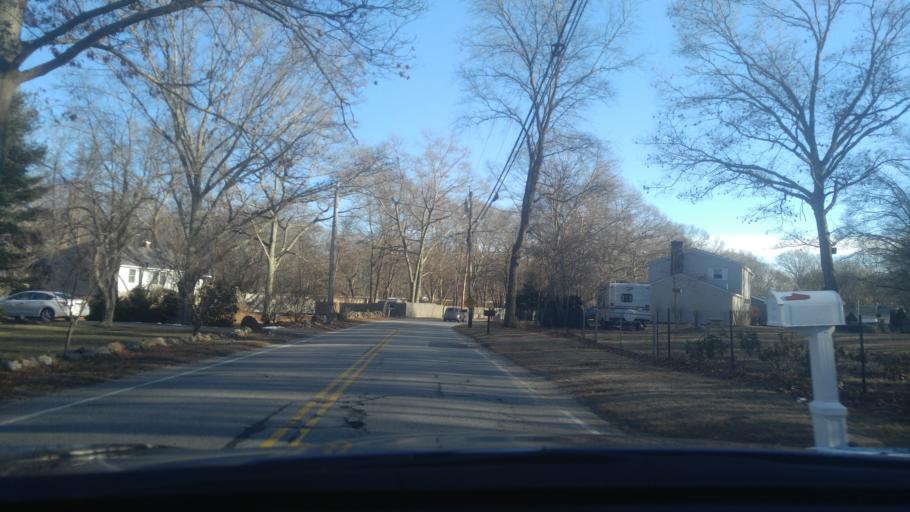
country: US
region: Rhode Island
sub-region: Washington County
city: North Kingstown
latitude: 41.5668
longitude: -71.4925
